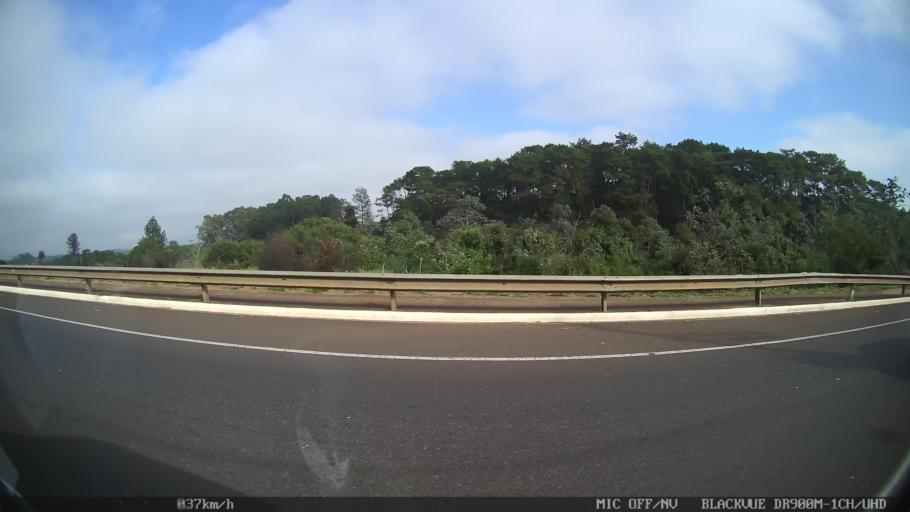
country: BR
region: Sao Paulo
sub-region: Sao Jose Do Rio Preto
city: Sao Jose do Rio Preto
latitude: -20.8168
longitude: -49.4343
